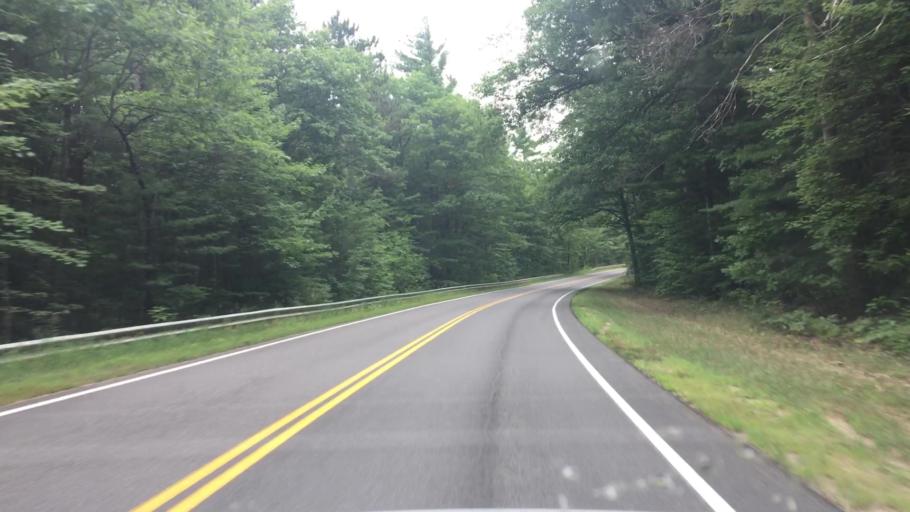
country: US
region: New York
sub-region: Clinton County
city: Morrisonville
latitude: 44.6176
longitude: -73.6207
